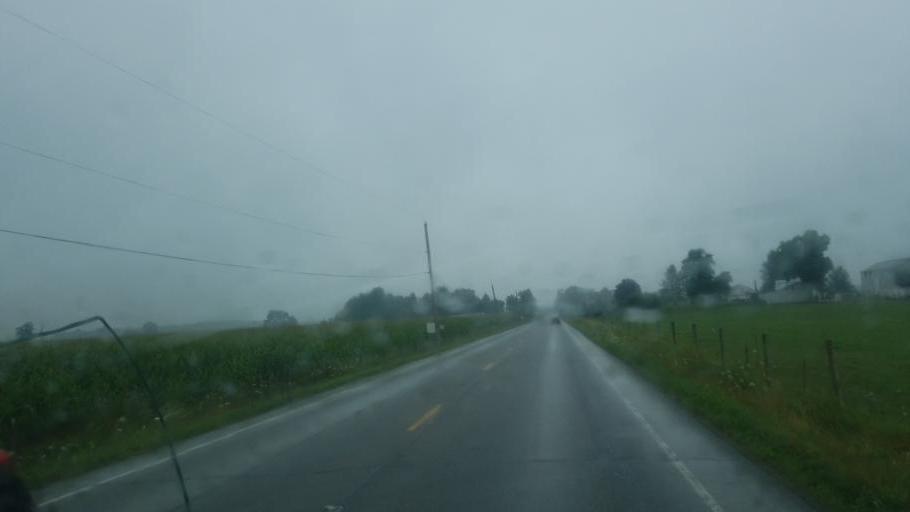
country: US
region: Indiana
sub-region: Allen County
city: Harlan
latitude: 41.1814
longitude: -84.9440
